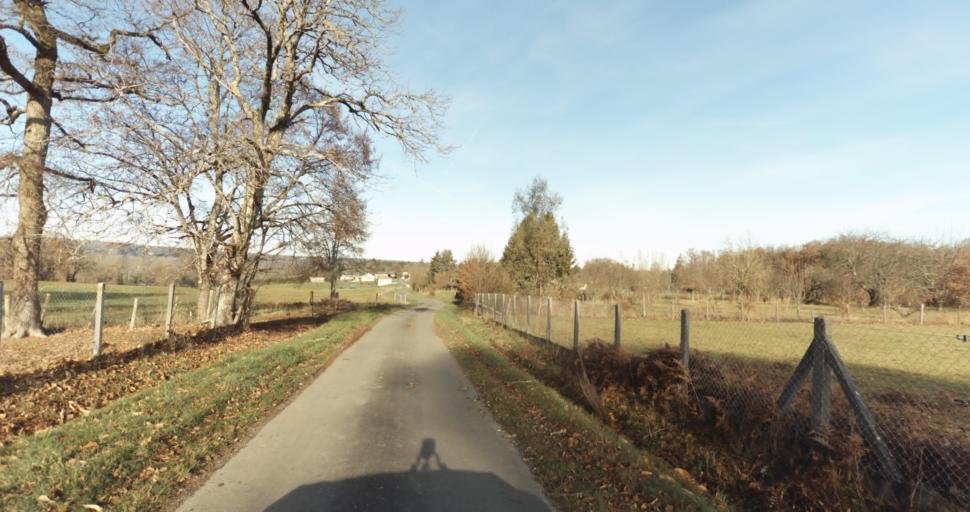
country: FR
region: Limousin
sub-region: Departement de la Haute-Vienne
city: Sereilhac
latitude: 45.7838
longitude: 1.0938
